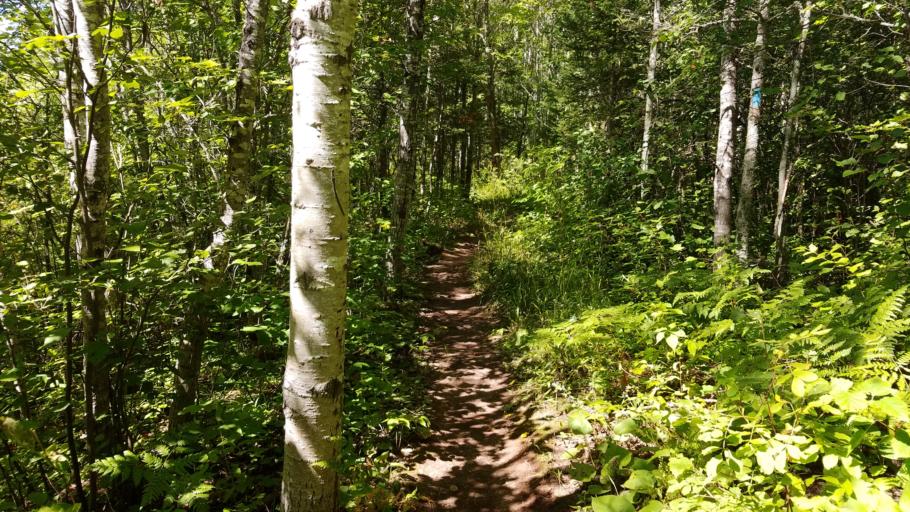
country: US
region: Michigan
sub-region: Ontonagon County
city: Ontonagon
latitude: 46.6510
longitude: -89.1572
